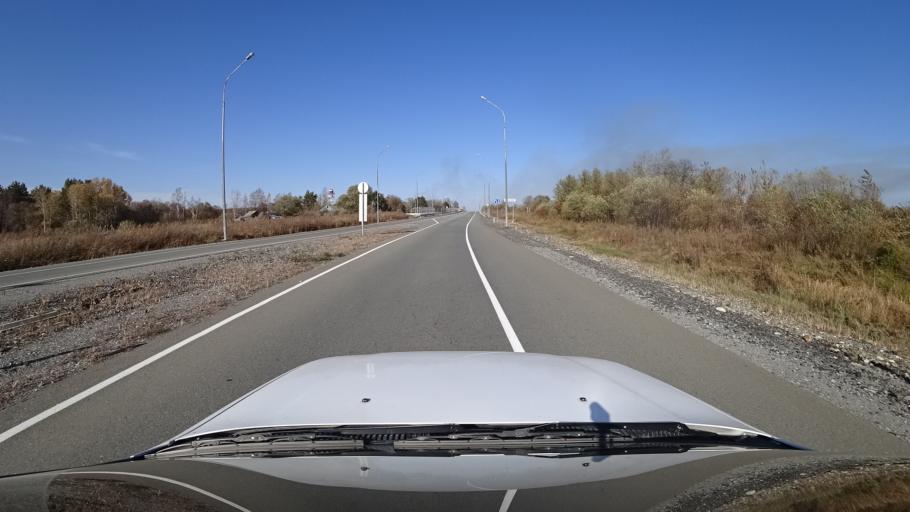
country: RU
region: Primorskiy
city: Dal'nerechensk
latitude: 45.8748
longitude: 133.7256
